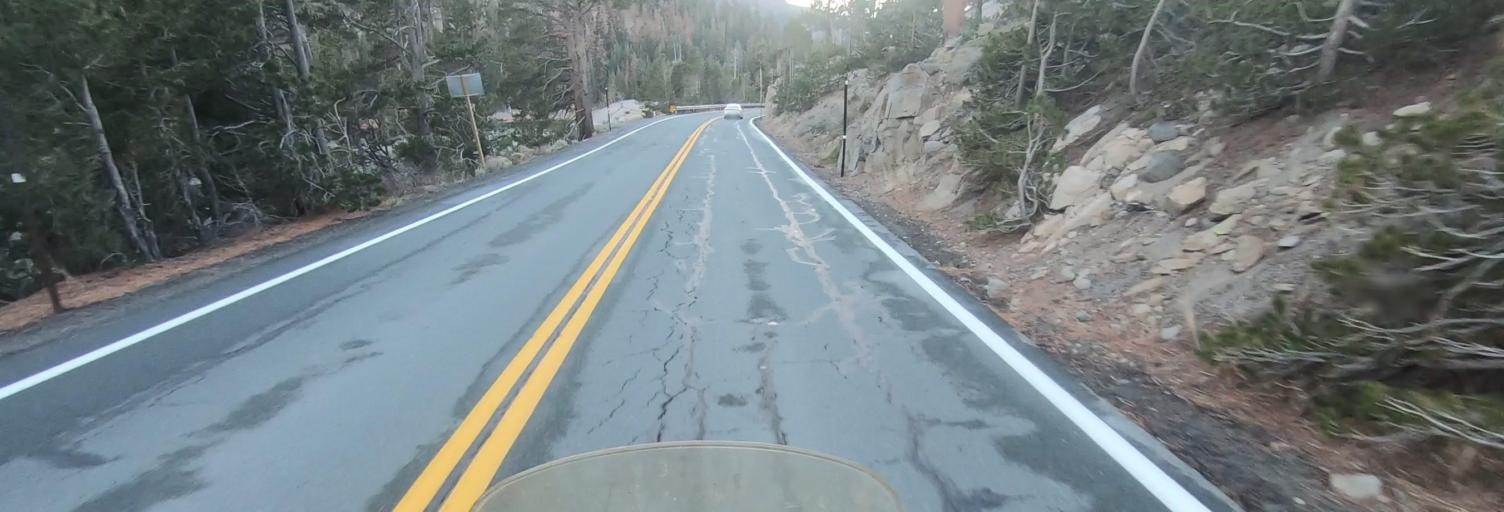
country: US
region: California
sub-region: El Dorado County
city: South Lake Tahoe
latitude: 38.7036
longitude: -120.0592
